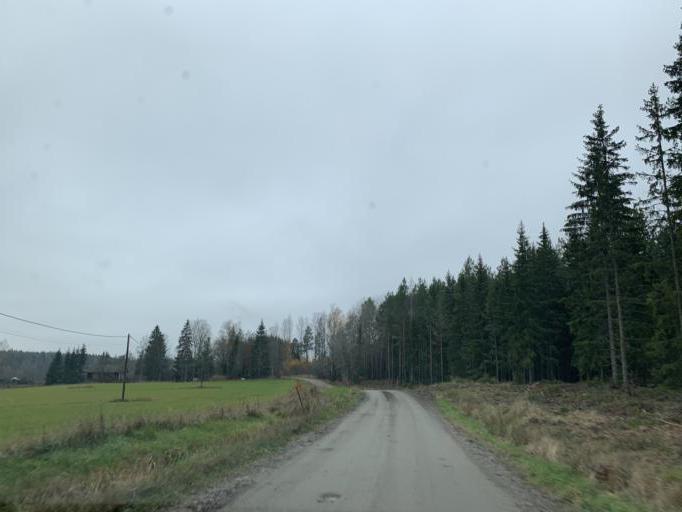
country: SE
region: Vaestmanland
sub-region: Surahammars Kommun
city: Ramnas
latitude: 59.7430
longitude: 16.1481
